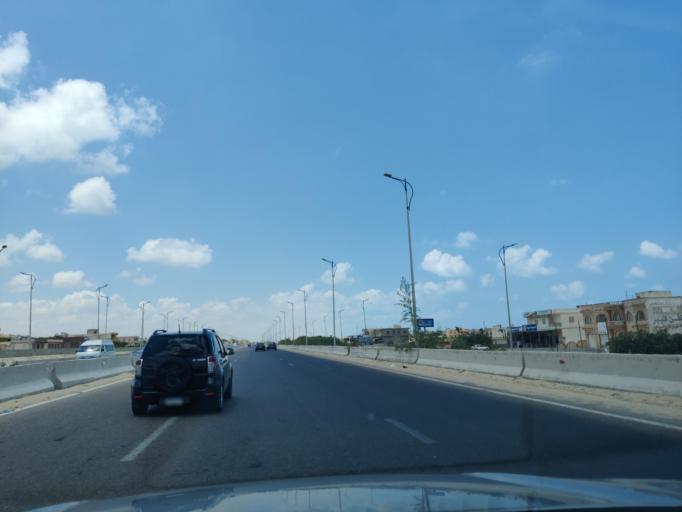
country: EG
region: Alexandria
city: Alexandria
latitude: 30.9963
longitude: 29.6045
